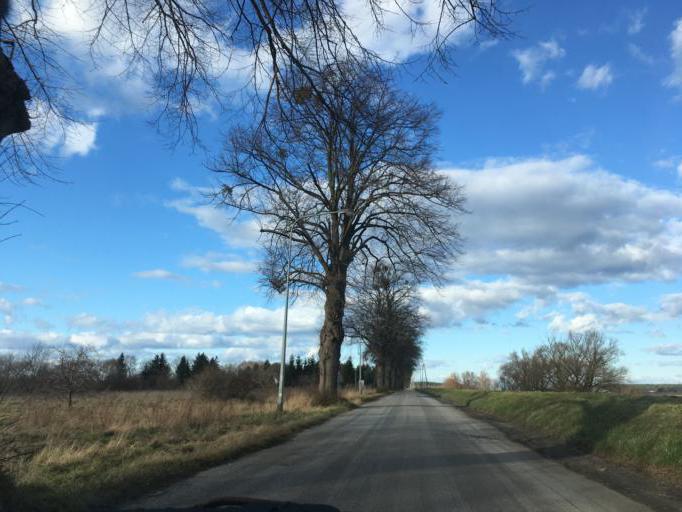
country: PL
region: Pomeranian Voivodeship
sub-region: Powiat nowodworski
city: Ostaszewo
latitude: 54.3154
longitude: 18.9307
